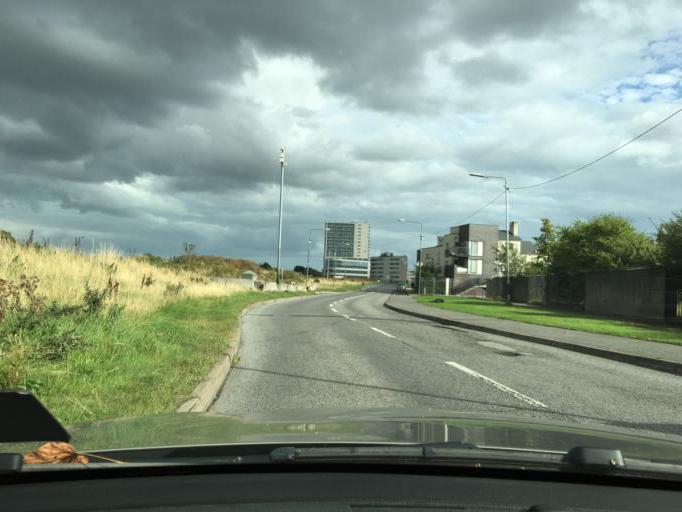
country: IE
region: Leinster
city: Ballymun
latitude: 53.4021
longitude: -6.2711
